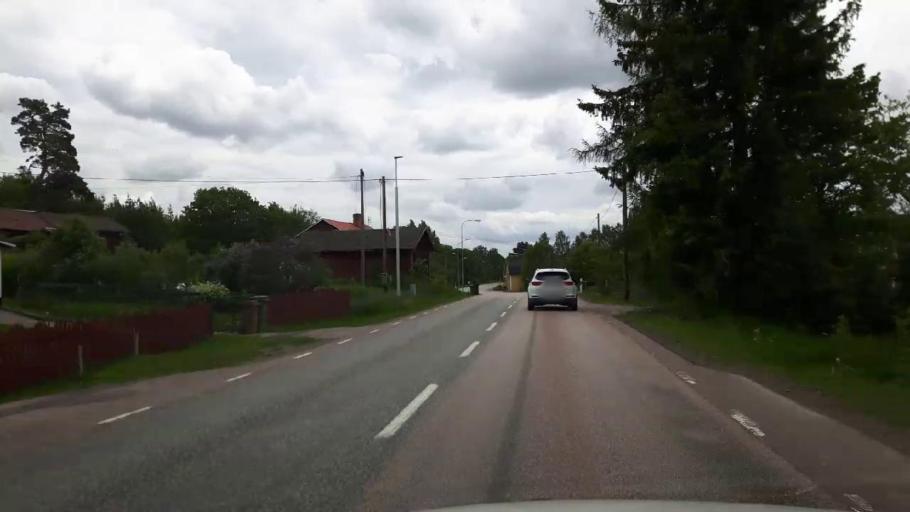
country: SE
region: Vaestmanland
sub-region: Norbergs Kommun
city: Norberg
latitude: 60.1031
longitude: 15.9260
